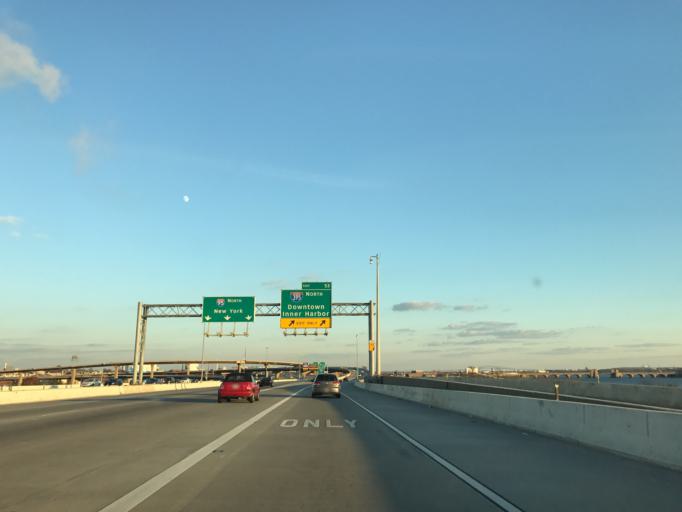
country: US
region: Maryland
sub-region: City of Baltimore
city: Baltimore
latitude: 39.2689
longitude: -76.6318
